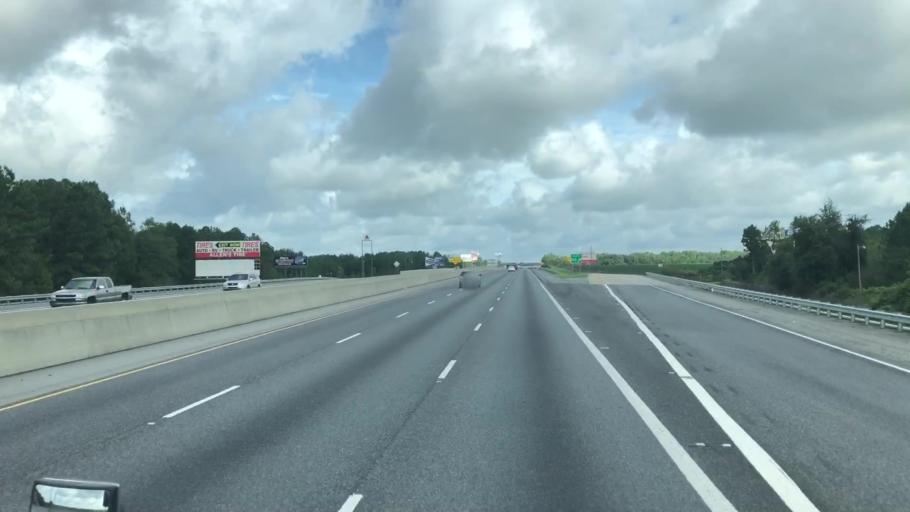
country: US
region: Georgia
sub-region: Turner County
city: Ashburn
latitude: 31.6782
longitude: -83.6176
